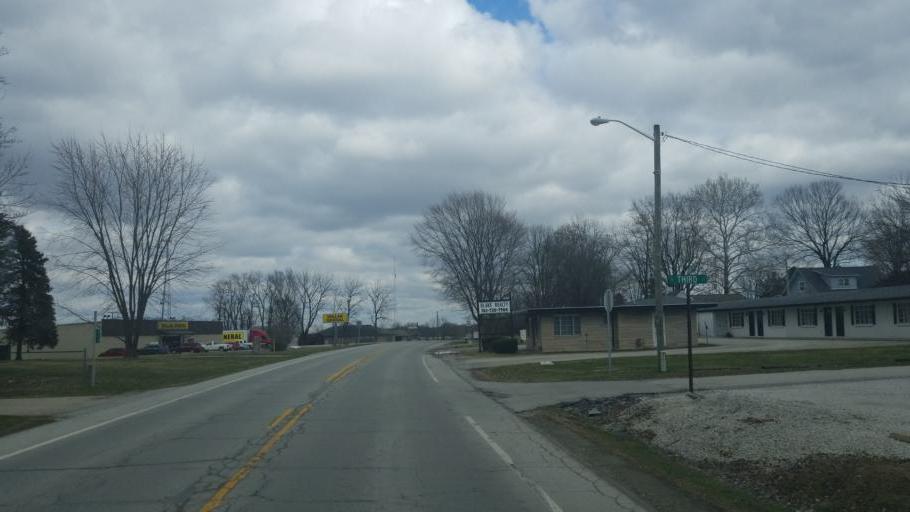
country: US
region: Indiana
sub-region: Putnam County
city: Greencastle
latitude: 39.7619
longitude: -86.8083
